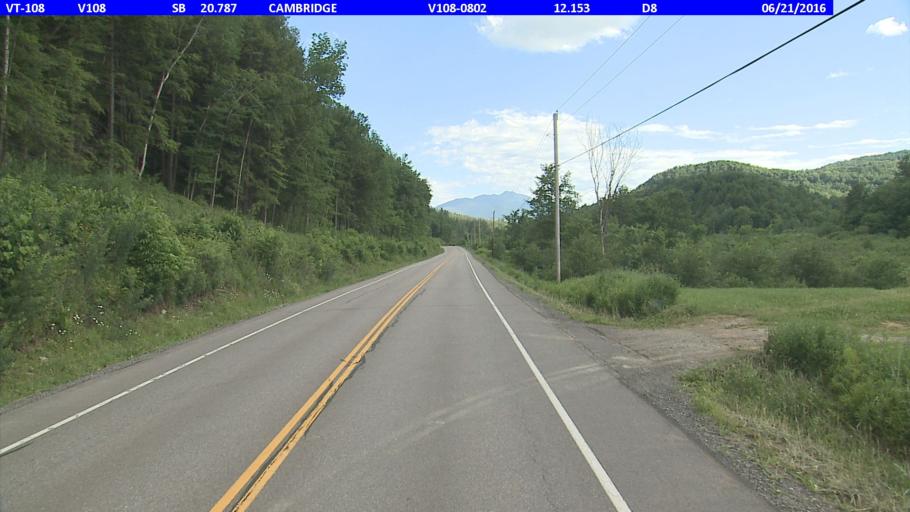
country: US
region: Vermont
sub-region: Lamoille County
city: Johnson
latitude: 44.6904
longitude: -72.8269
